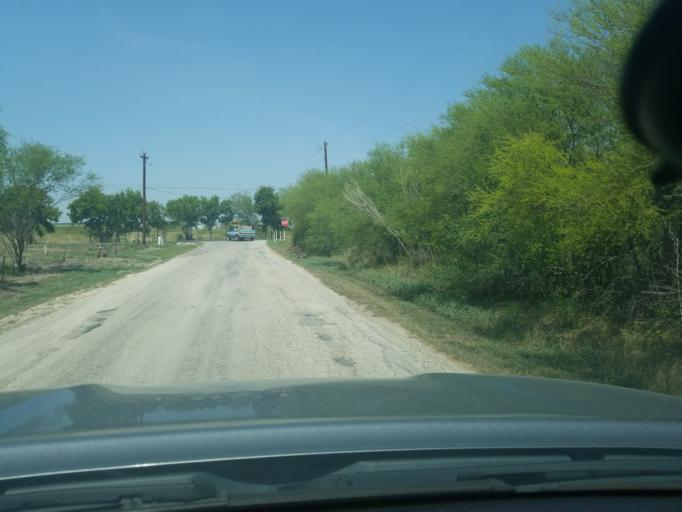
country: US
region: Texas
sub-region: Guadalupe County
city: Marion
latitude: 29.5806
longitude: -98.1701
